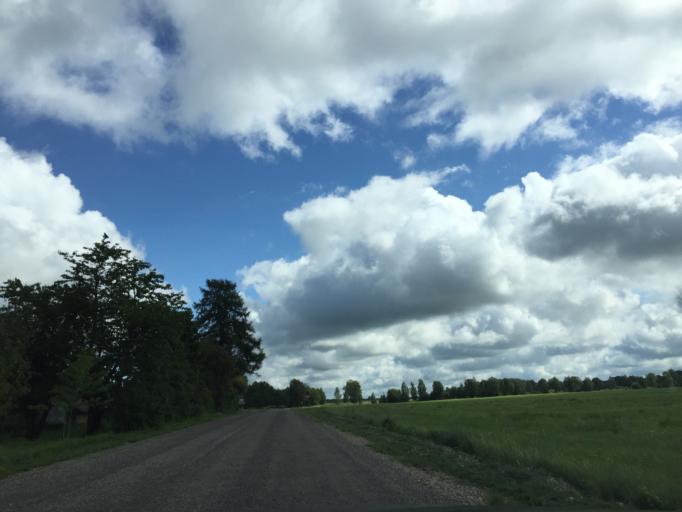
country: LV
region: Ligatne
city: Ligatne
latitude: 57.2014
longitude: 24.9512
